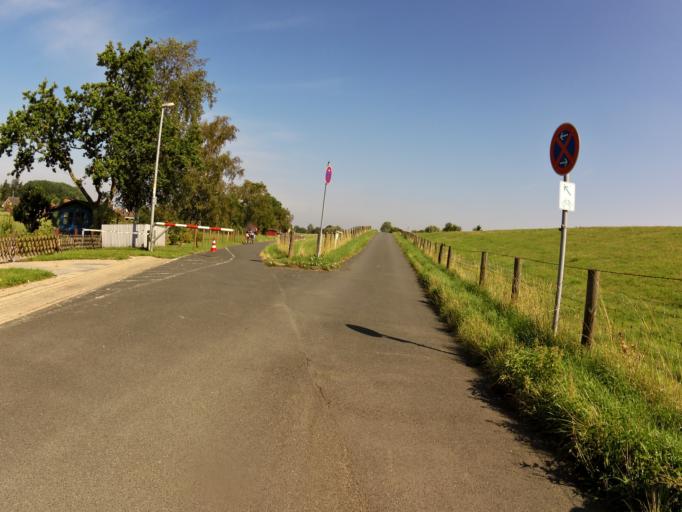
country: DE
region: Lower Saxony
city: Elsfleth
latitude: 53.2550
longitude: 8.4744
